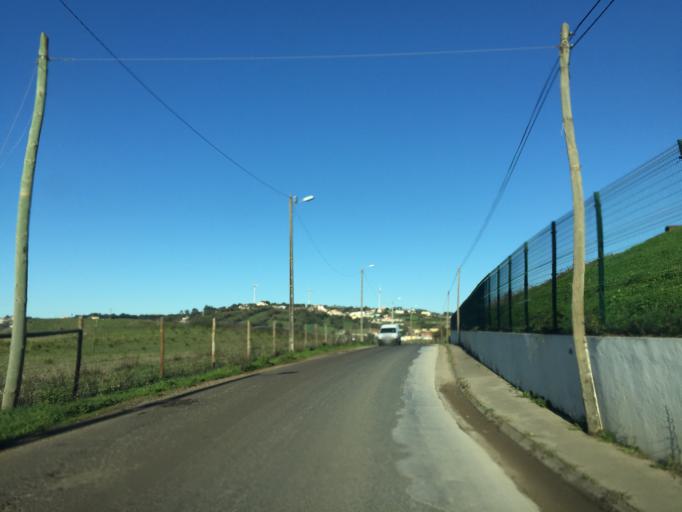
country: PT
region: Lisbon
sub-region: Odivelas
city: Canecas
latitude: 38.8285
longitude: -9.2480
